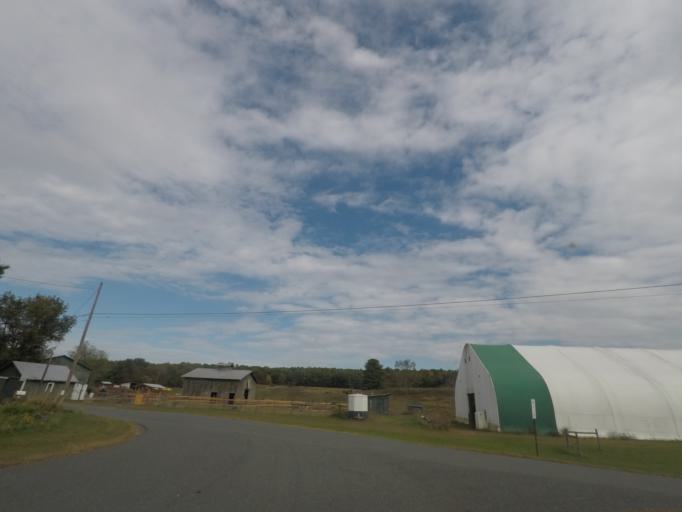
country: US
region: New York
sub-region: Rensselaer County
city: Nassau
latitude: 42.5434
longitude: -73.6255
